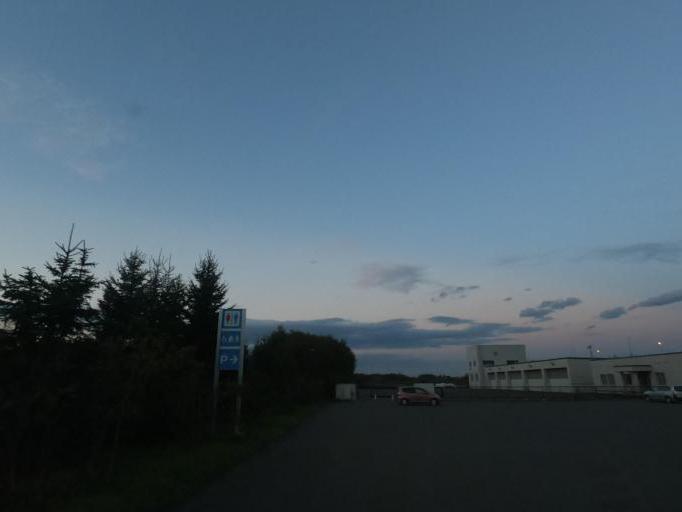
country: JP
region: Hokkaido
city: Obihiro
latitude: 42.6914
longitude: 143.1529
